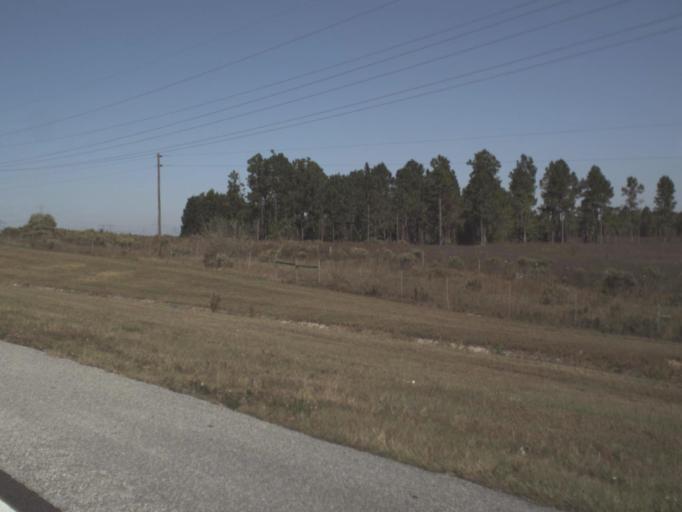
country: US
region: Florida
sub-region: Lake County
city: Hawthorne
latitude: 28.7693
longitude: -81.9533
